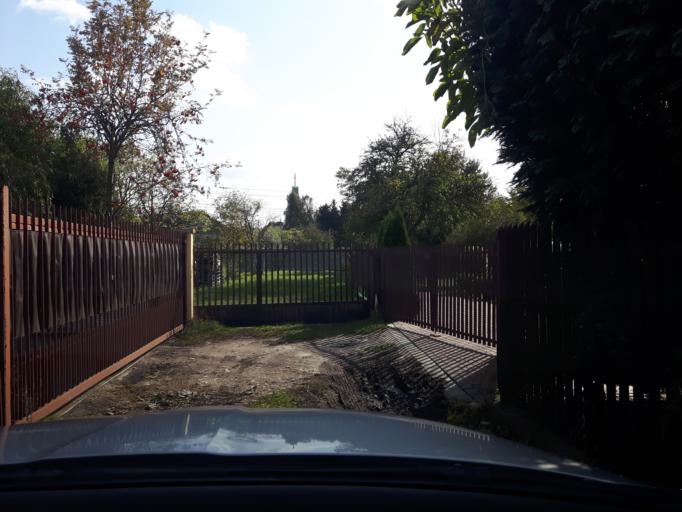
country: PL
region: Masovian Voivodeship
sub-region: Powiat wolominski
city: Zabki
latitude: 52.2901
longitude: 21.1061
